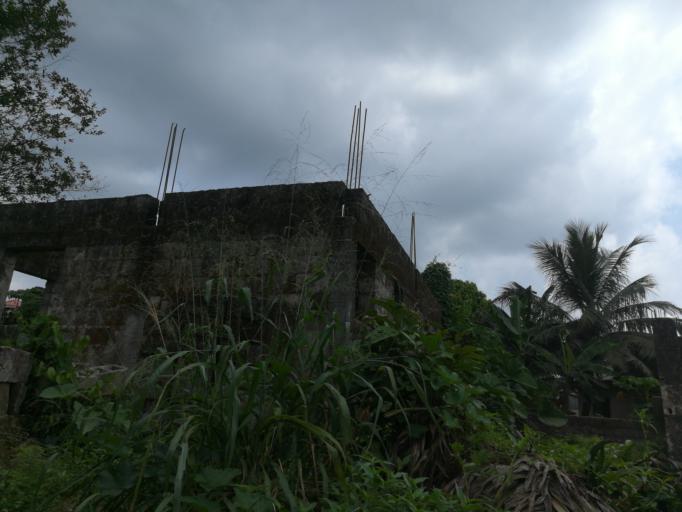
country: NG
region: Rivers
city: Okrika
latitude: 4.7314
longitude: 7.1442
